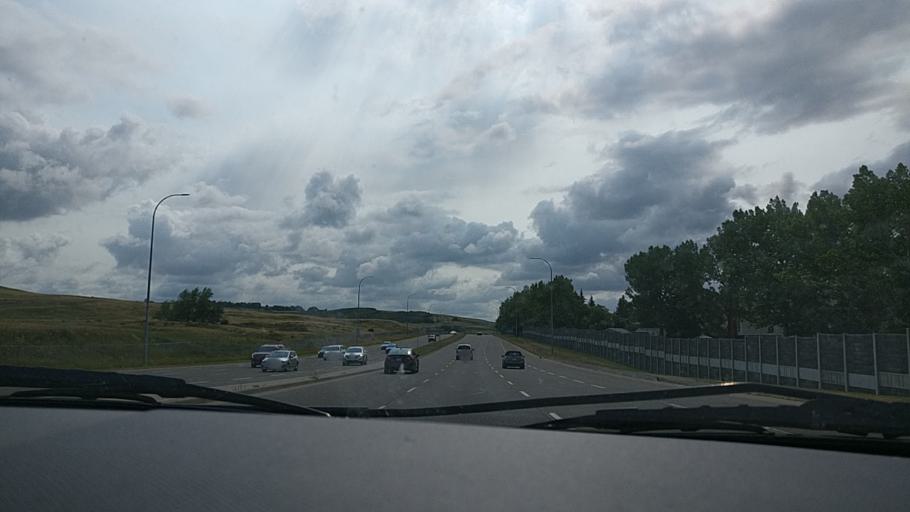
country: CA
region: Alberta
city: Calgary
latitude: 51.1083
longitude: -114.1384
